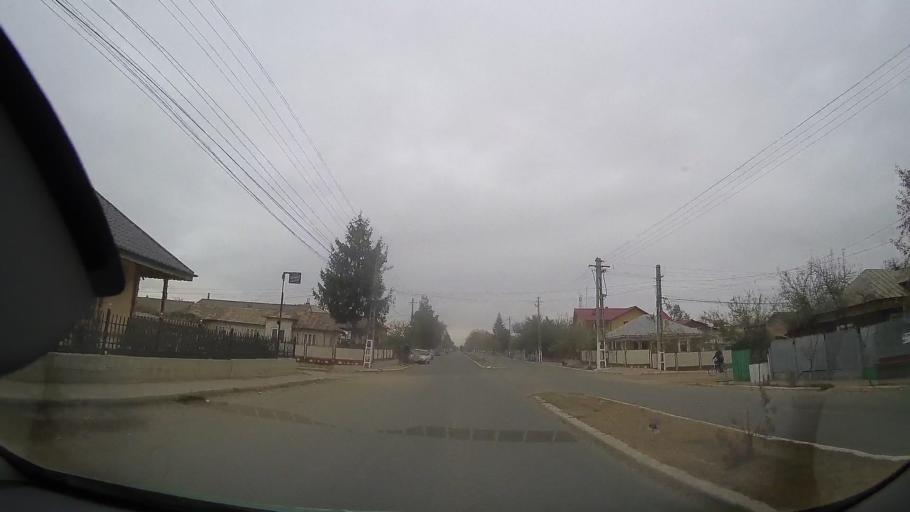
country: RO
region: Buzau
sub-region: Comuna Rusetu
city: Rusetu
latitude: 44.9583
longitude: 27.2151
